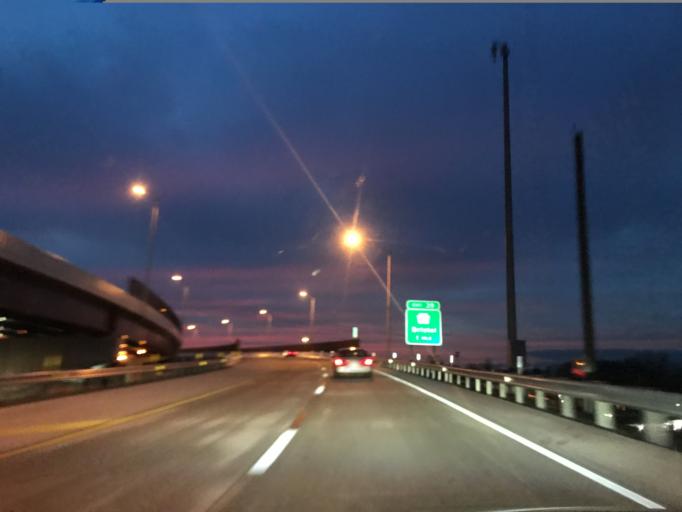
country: US
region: Pennsylvania
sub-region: Bucks County
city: Hulmeville
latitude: 40.1285
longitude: -74.8826
